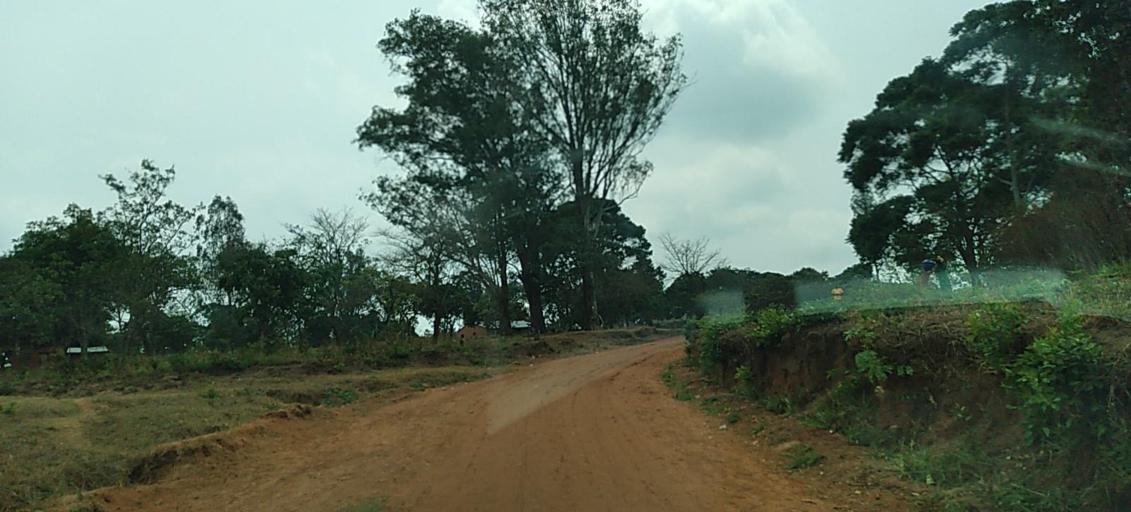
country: ZM
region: North-Western
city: Mwinilunga
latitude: -11.4417
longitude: 24.7469
